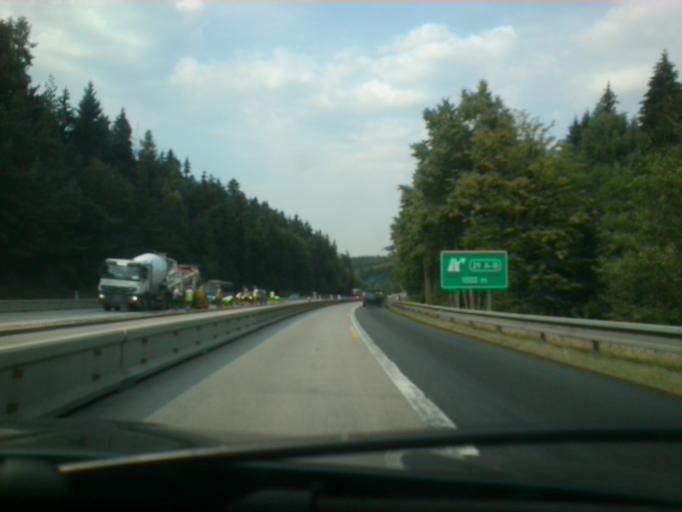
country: CZ
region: Central Bohemia
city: Ondrejov
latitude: 49.8489
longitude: 14.7969
